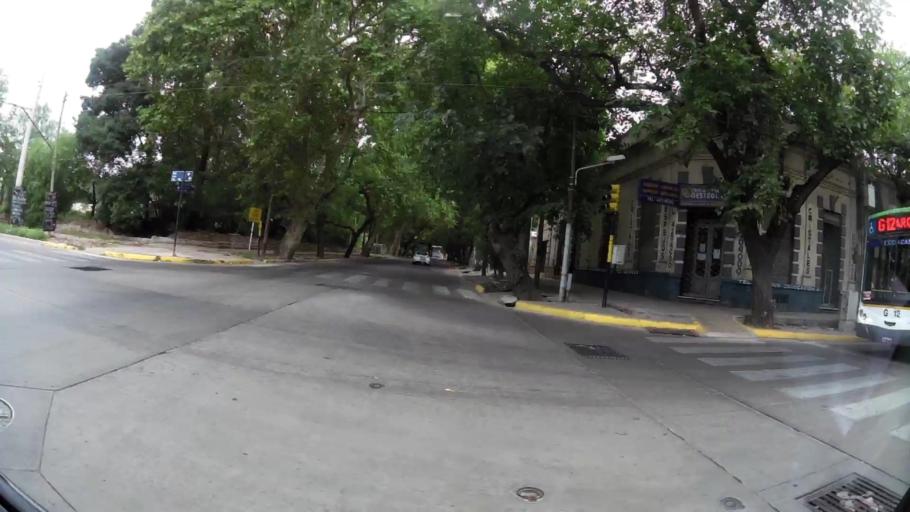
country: AR
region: Mendoza
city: Mendoza
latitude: -32.8790
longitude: -68.8457
